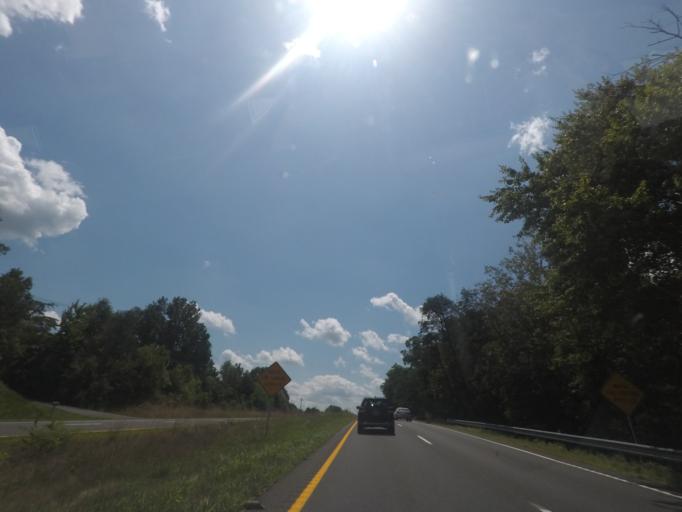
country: US
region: Virginia
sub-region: City of Winchester
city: Winchester
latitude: 39.1335
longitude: -78.1208
